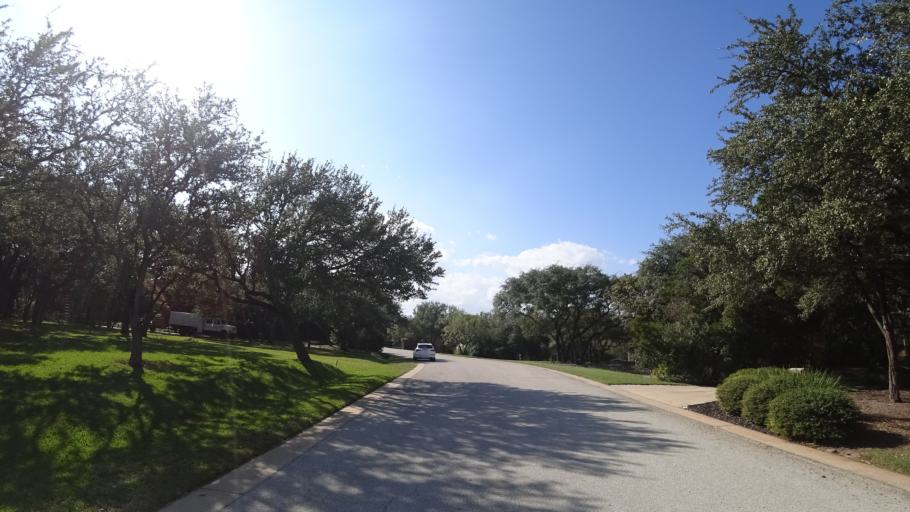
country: US
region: Texas
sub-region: Travis County
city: Lost Creek
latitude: 30.3074
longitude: -97.8582
